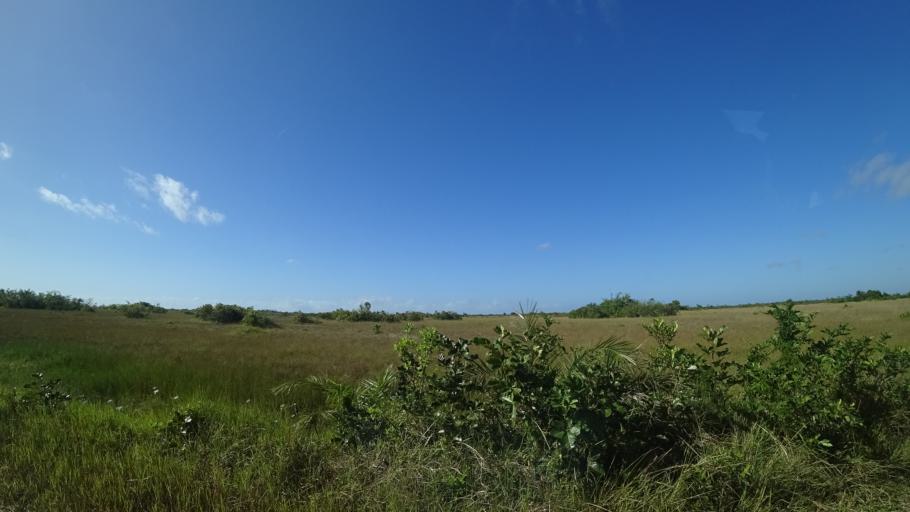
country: MZ
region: Sofala
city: Beira
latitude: -19.6959
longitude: 35.0337
